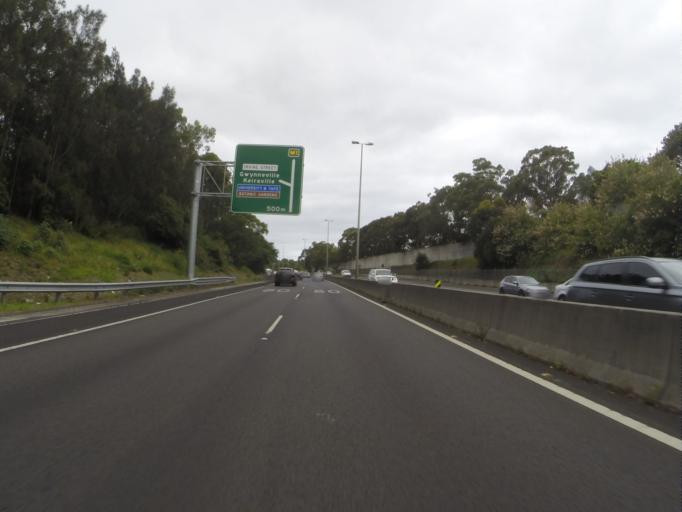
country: AU
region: New South Wales
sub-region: Wollongong
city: Gwynneville
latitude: -34.4155
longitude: 150.8804
